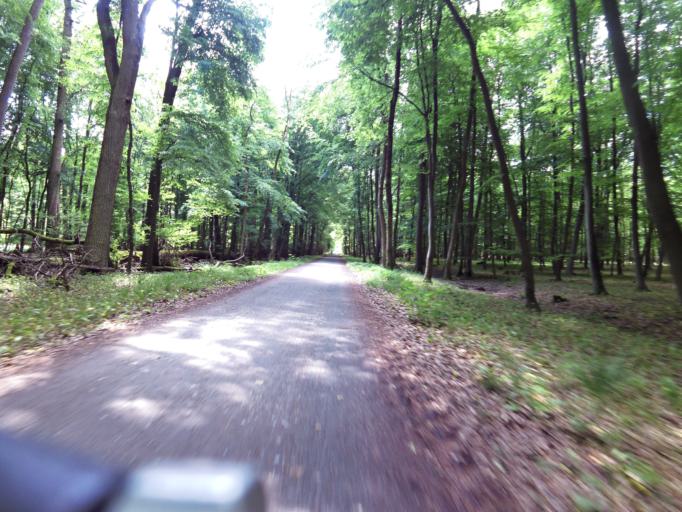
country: DE
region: Hesse
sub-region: Regierungsbezirk Darmstadt
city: Nauheim
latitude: 49.9883
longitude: 8.5116
